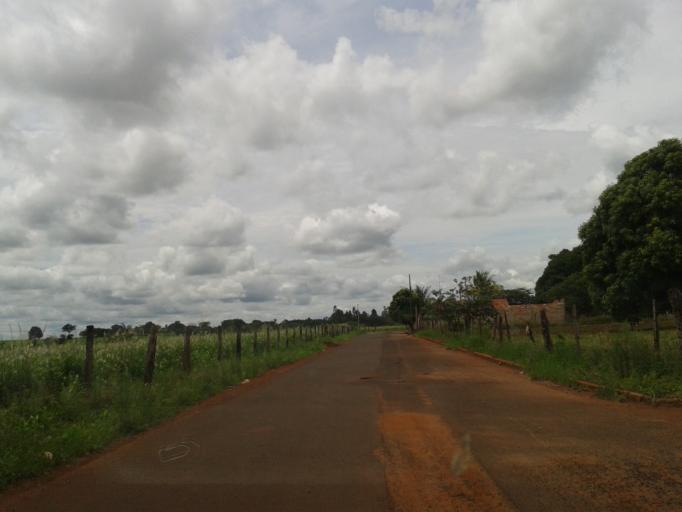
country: BR
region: Minas Gerais
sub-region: Centralina
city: Centralina
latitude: -18.5789
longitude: -49.2075
